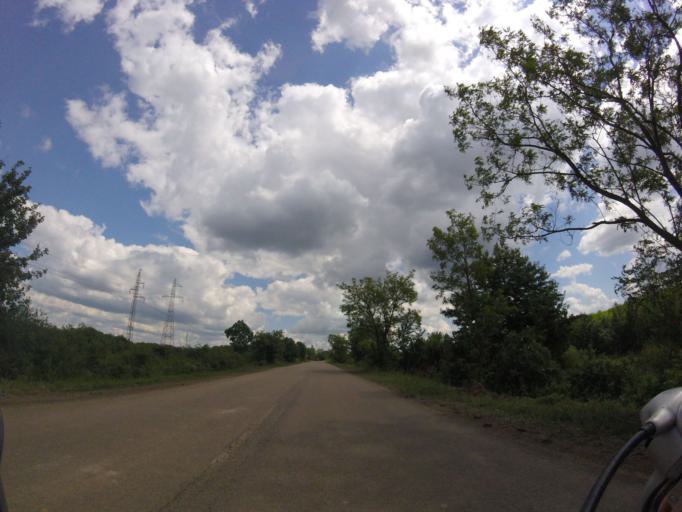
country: HU
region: Heves
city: Domoszlo
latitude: 47.7718
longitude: 20.1125
